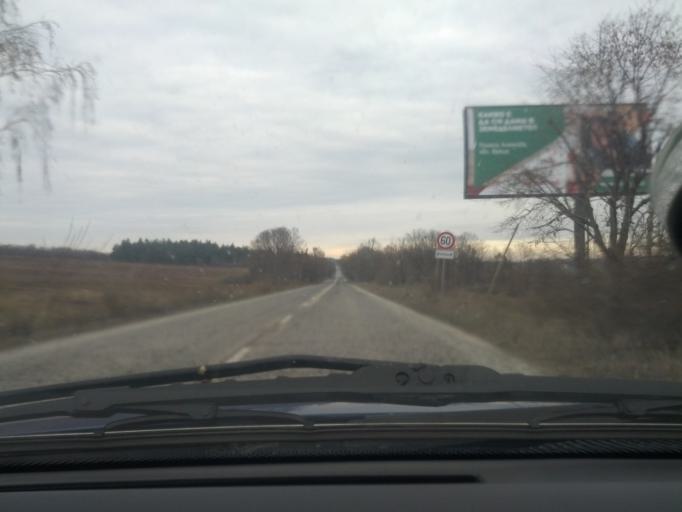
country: BG
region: Vratsa
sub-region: Obshtina Vratsa
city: Vratsa
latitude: 43.2959
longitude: 23.6580
